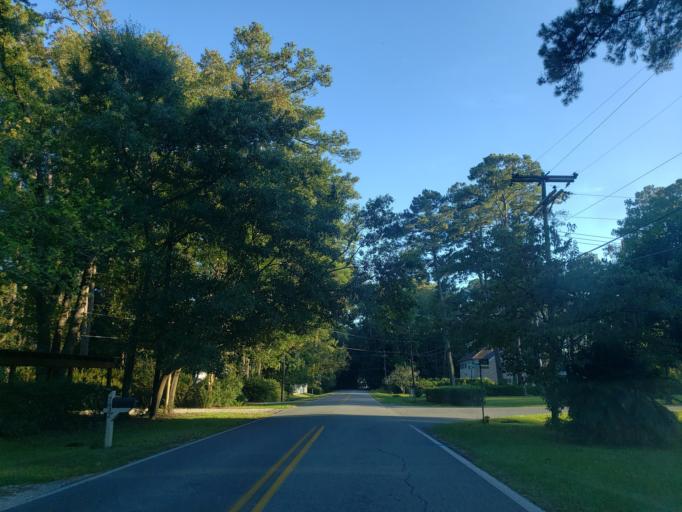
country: US
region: Georgia
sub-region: Chatham County
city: Isle of Hope
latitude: 31.9862
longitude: -81.0544
